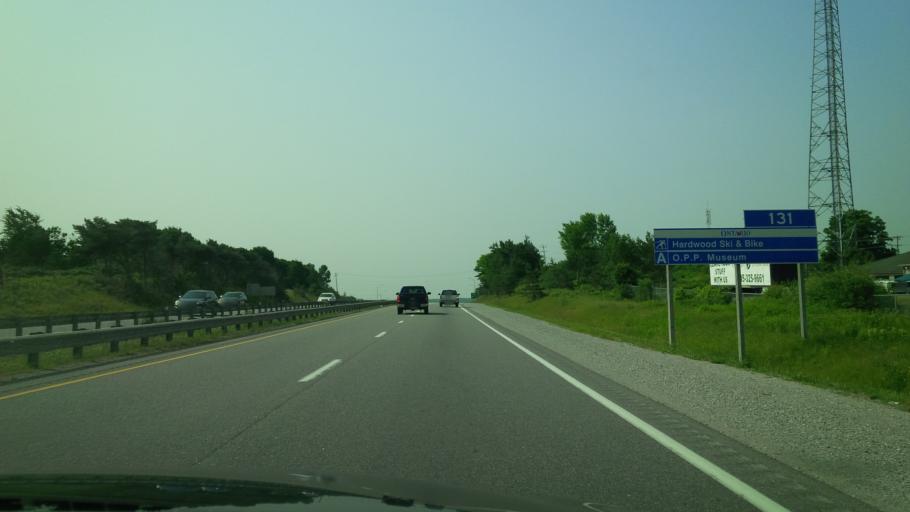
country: CA
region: Ontario
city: Orillia
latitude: 44.5968
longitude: -79.4474
